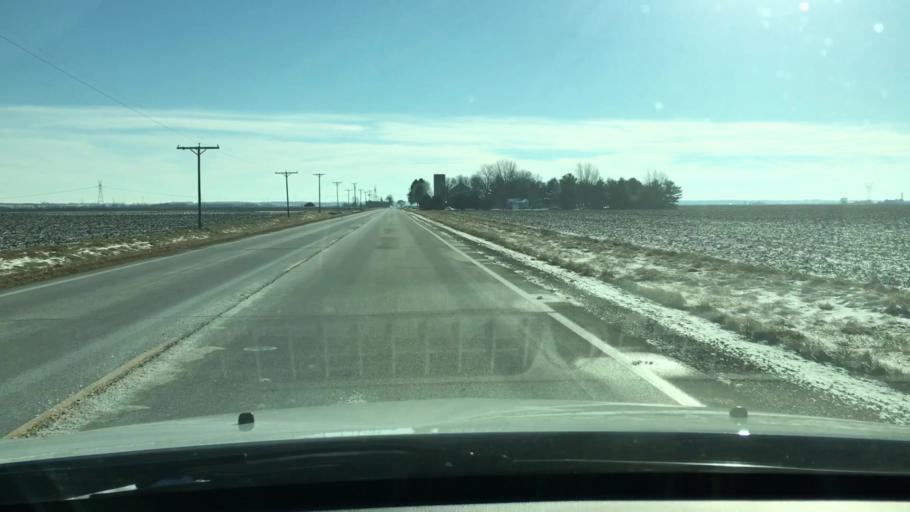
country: US
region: Illinois
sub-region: Ogle County
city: Rochelle
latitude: 41.8100
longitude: -89.0834
